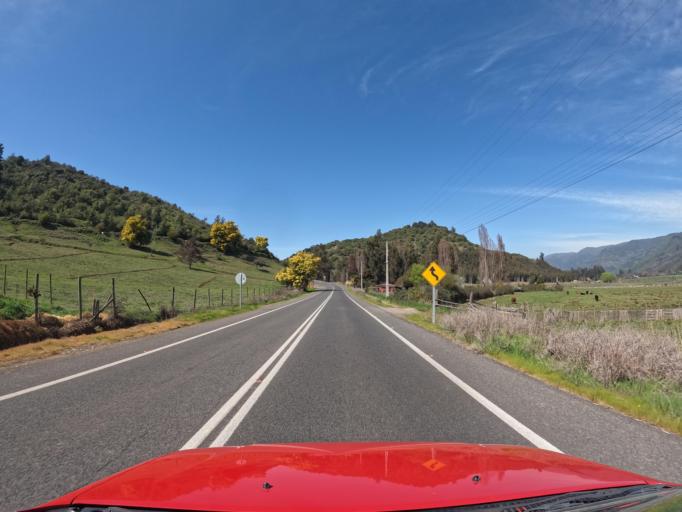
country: CL
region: Maule
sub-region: Provincia de Curico
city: Teno
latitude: -34.9784
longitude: -70.9709
